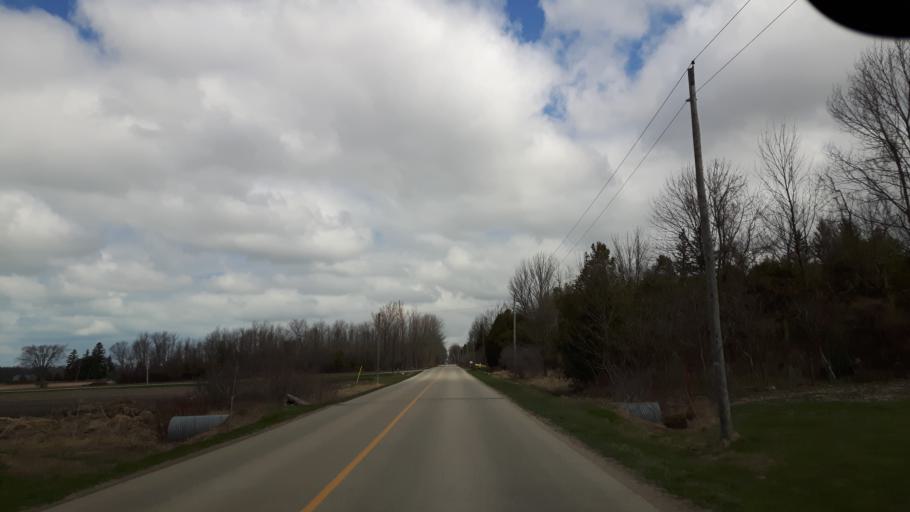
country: CA
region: Ontario
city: Goderich
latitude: 43.6848
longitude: -81.6847
